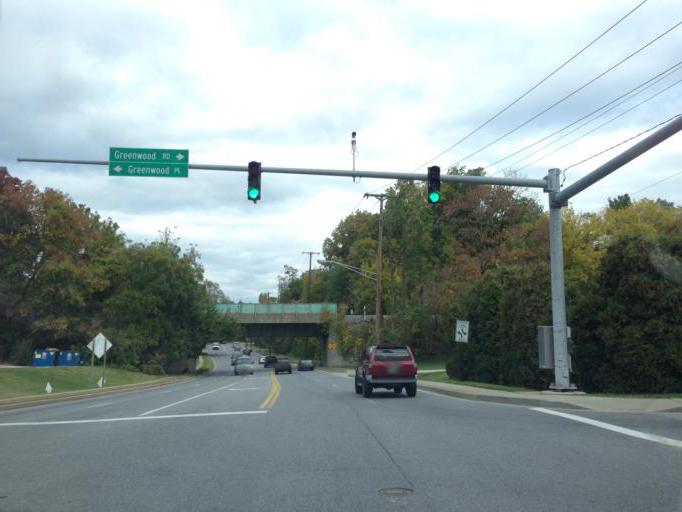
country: US
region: Maryland
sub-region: Baltimore County
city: Pikesville
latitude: 39.3737
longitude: -76.7397
